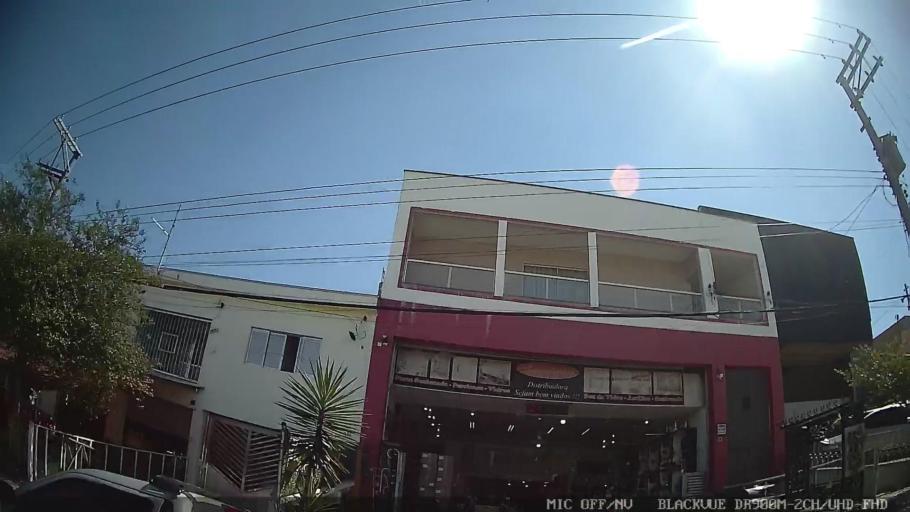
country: BR
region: Sao Paulo
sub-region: Sao Caetano Do Sul
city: Sao Caetano do Sul
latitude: -23.5861
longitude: -46.5180
